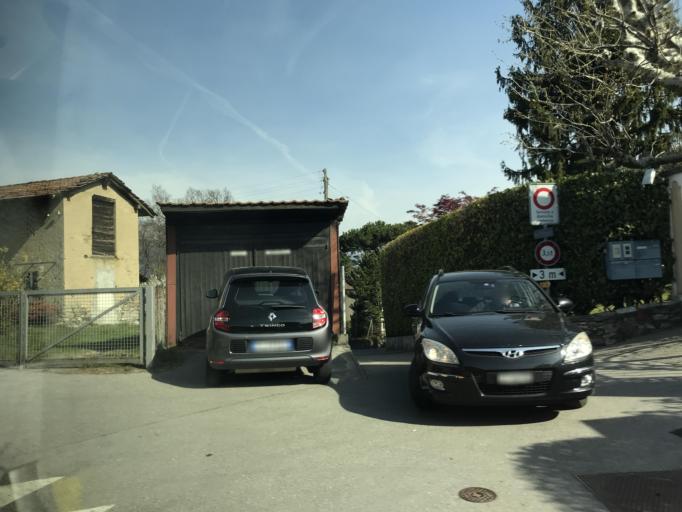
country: CH
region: Ticino
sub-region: Lugano District
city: Montagnola
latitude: 45.9879
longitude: 8.9235
